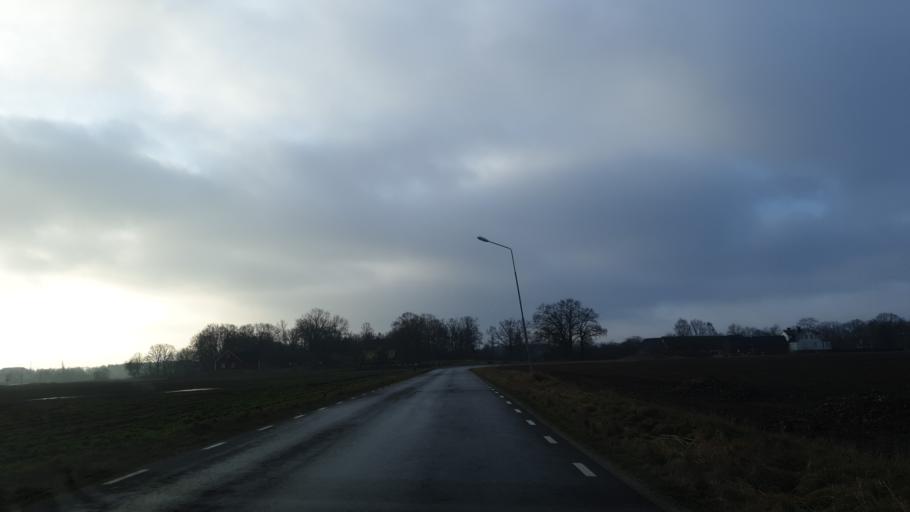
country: SE
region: Blekinge
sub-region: Karlshamns Kommun
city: Morrum
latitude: 56.1649
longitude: 14.7578
